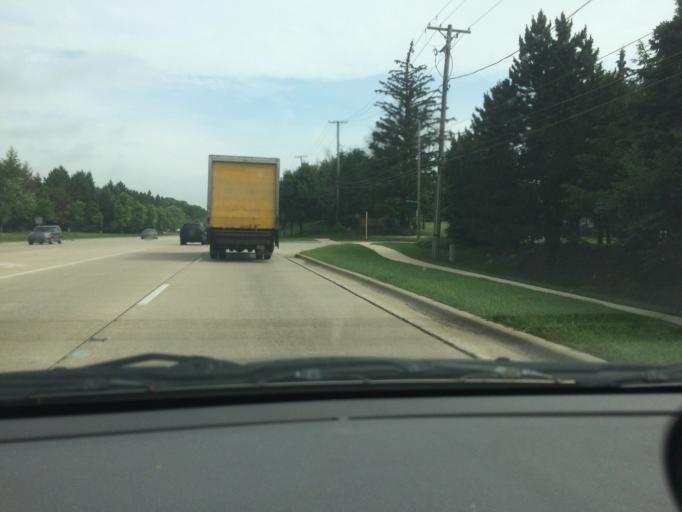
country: US
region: Illinois
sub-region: Cook County
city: Bartlett
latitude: 42.0129
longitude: -88.2031
